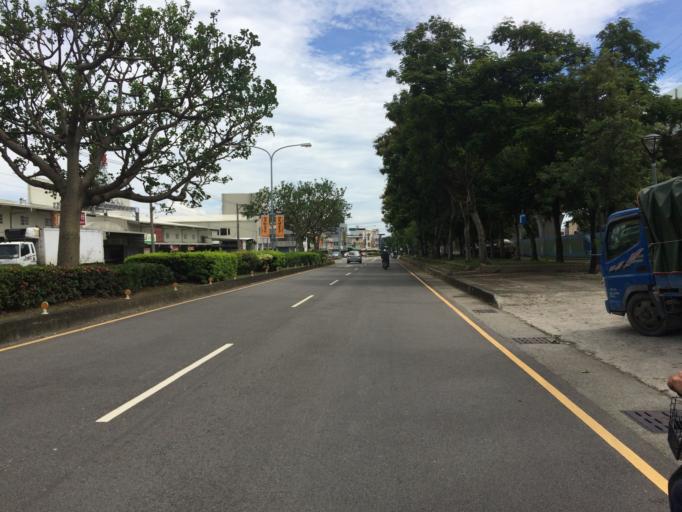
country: TW
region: Taiwan
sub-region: Taichung City
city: Taichung
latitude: 24.1461
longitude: 120.6976
